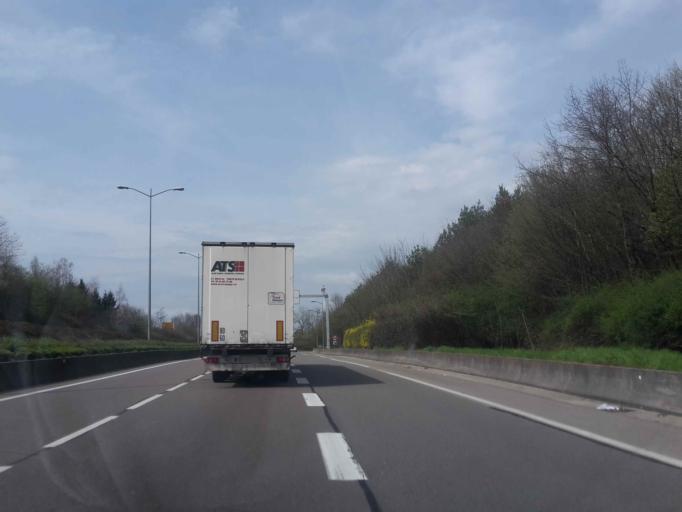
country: FR
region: Franche-Comte
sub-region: Departement du Doubs
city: Besancon
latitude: 47.2699
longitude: 6.0013
